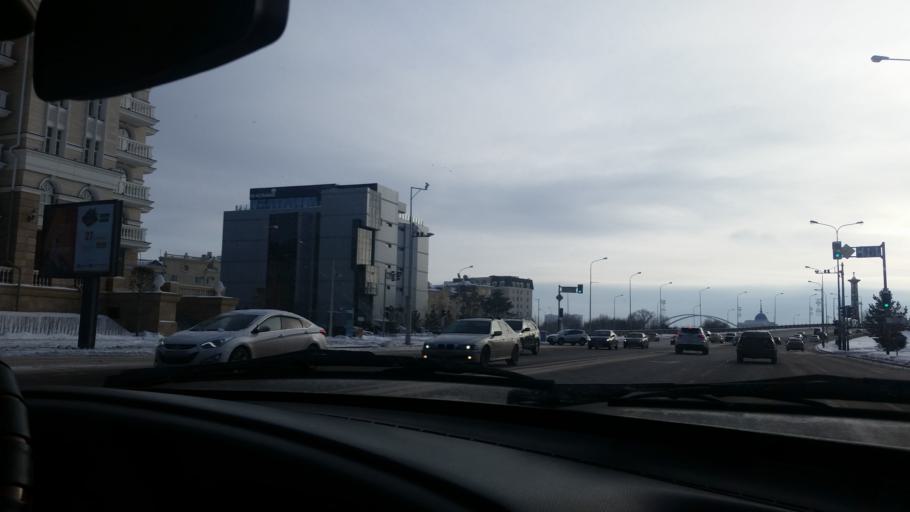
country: KZ
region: Astana Qalasy
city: Astana
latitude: 51.1422
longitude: 71.4452
